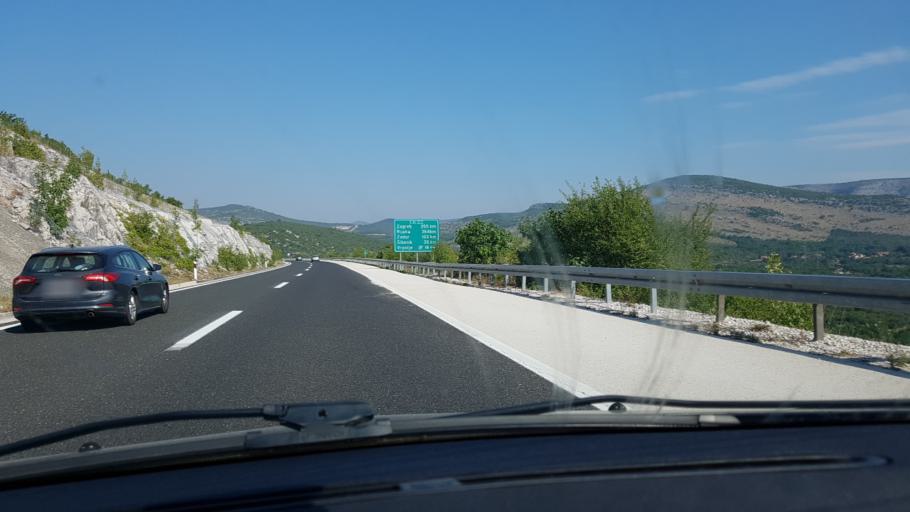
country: HR
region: Splitsko-Dalmatinska
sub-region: Grad Trogir
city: Trogir
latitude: 43.6286
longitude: 16.2321
